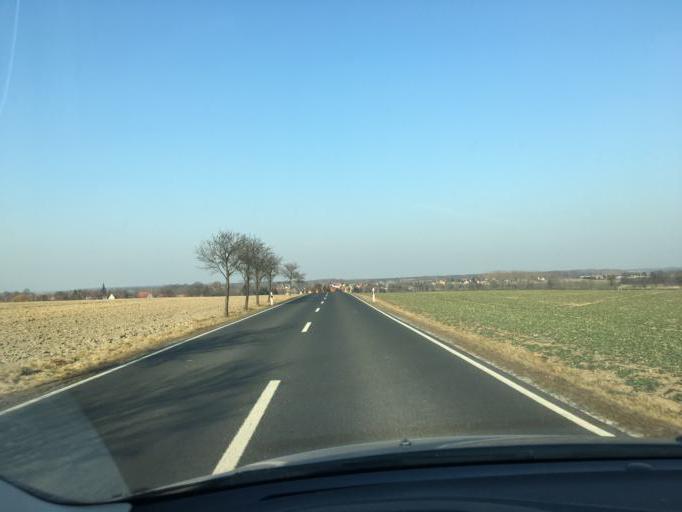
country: DE
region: Saxony
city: Kitzscher
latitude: 51.1155
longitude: 12.5849
